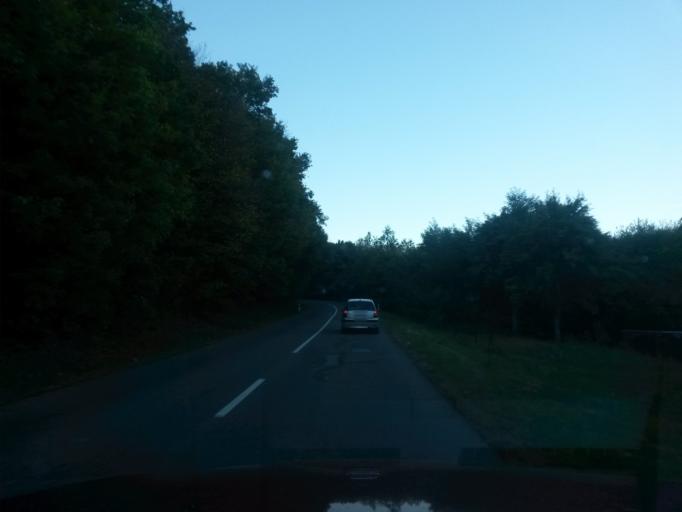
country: SK
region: Kosicky
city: Sobrance
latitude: 48.7856
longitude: 22.2488
